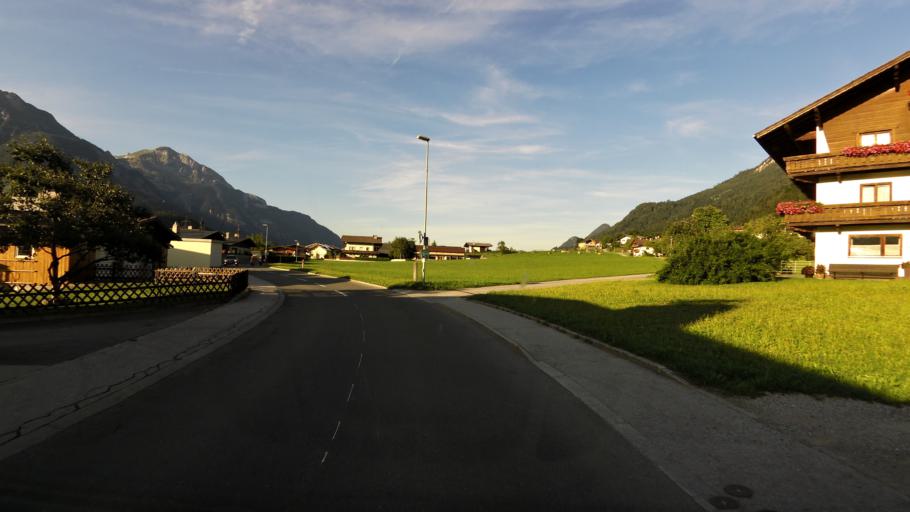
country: AT
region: Tyrol
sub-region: Politischer Bezirk Schwaz
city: Gallzein
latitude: 47.3779
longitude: 11.7697
